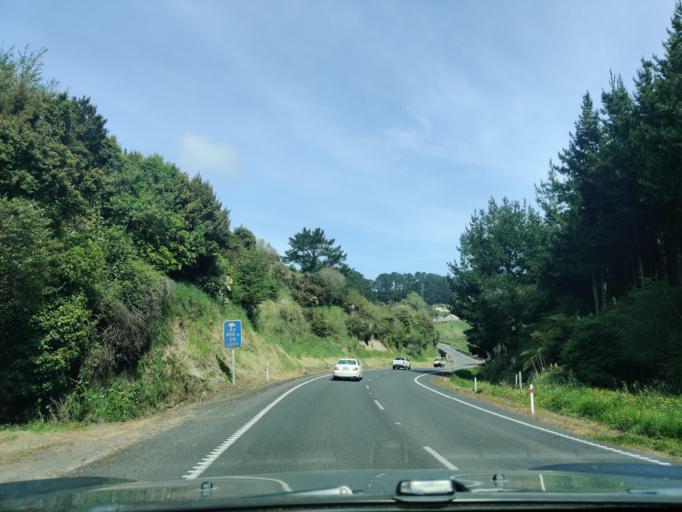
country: NZ
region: Taranaki
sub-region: South Taranaki District
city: Hawera
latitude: -39.6383
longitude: 174.3767
